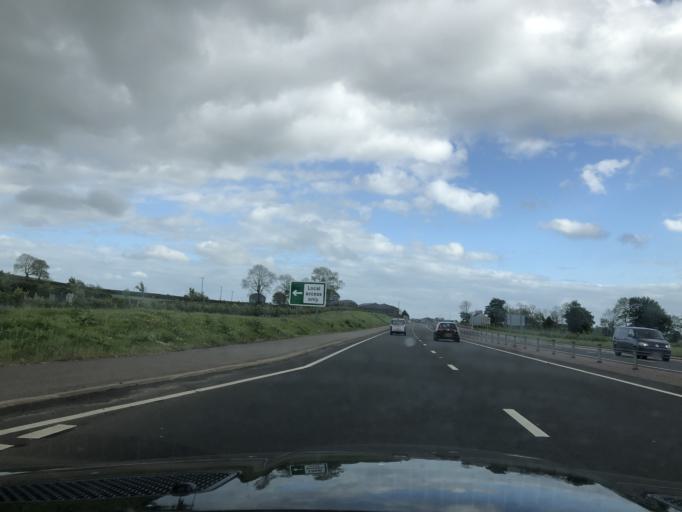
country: GB
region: Northern Ireland
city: Dunloy
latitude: 55.0108
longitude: -6.3634
